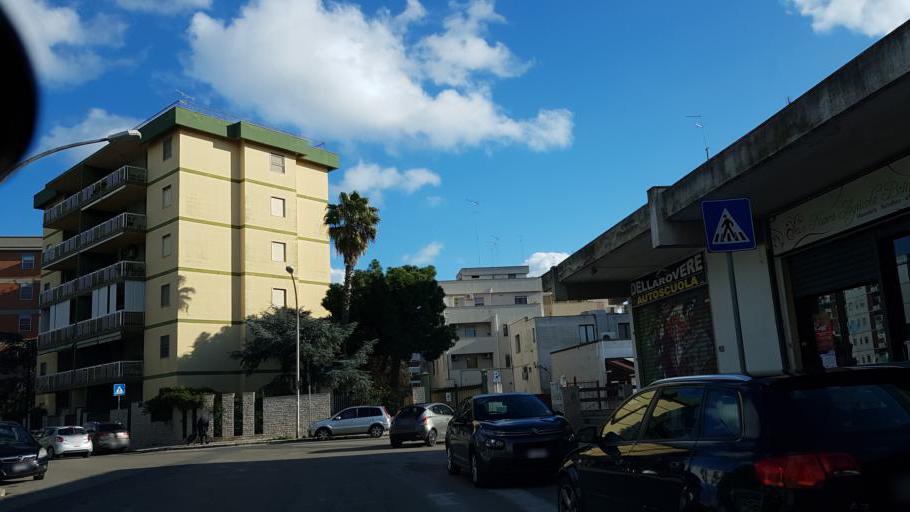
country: IT
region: Apulia
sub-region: Provincia di Brindisi
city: Brindisi
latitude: 40.6245
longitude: 17.9266
